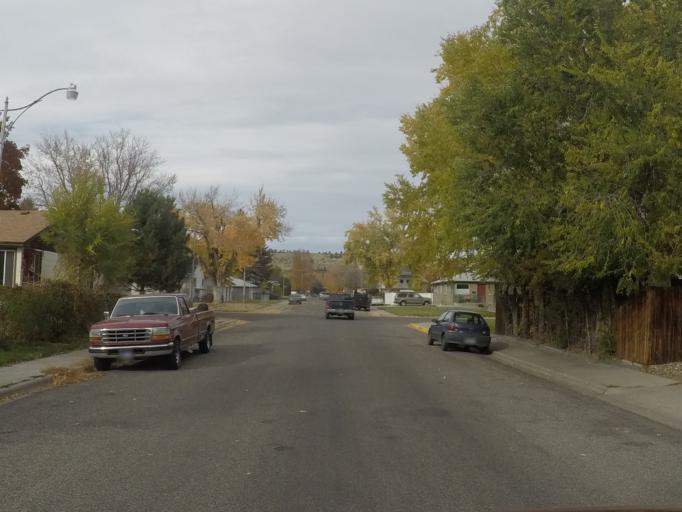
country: US
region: Montana
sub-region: Yellowstone County
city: Billings
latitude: 45.7876
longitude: -108.5512
